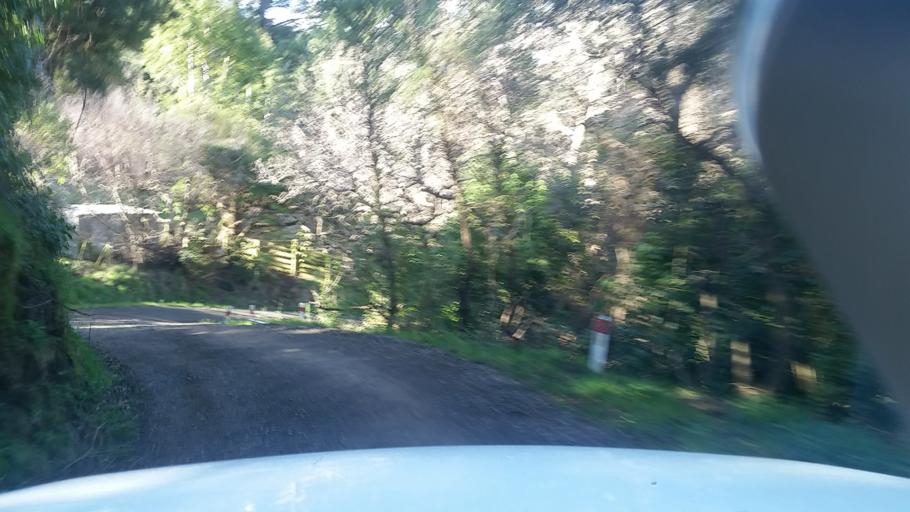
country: NZ
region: Canterbury
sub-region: Christchurch City
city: Christchurch
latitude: -43.7751
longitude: 172.9815
